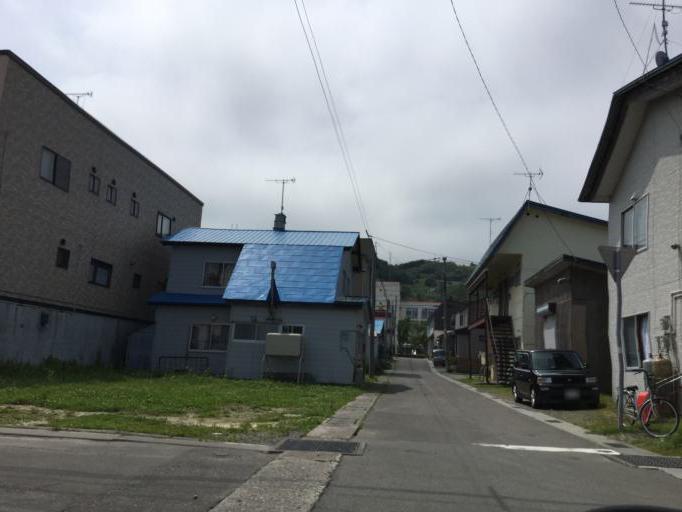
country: JP
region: Hokkaido
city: Wakkanai
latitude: 45.4265
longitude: 141.6719
